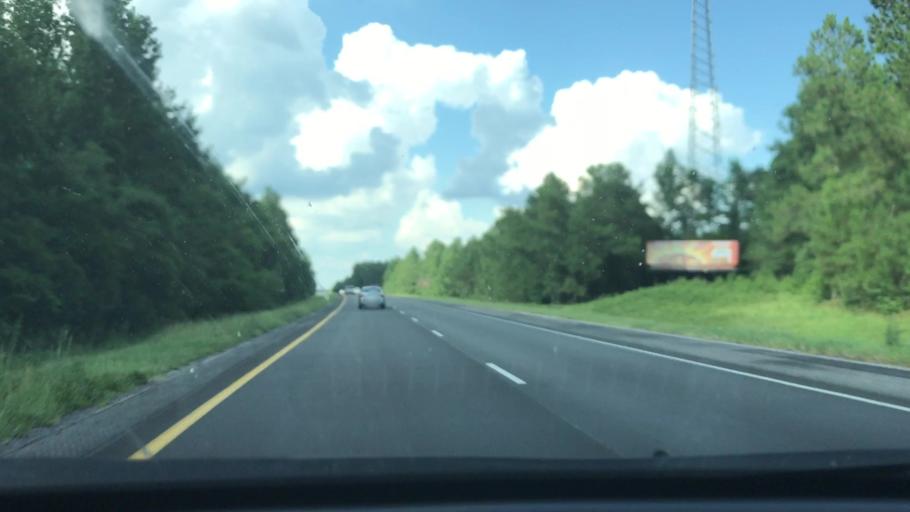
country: US
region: South Carolina
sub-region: Clarendon County
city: Manning
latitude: 33.8447
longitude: -80.1220
